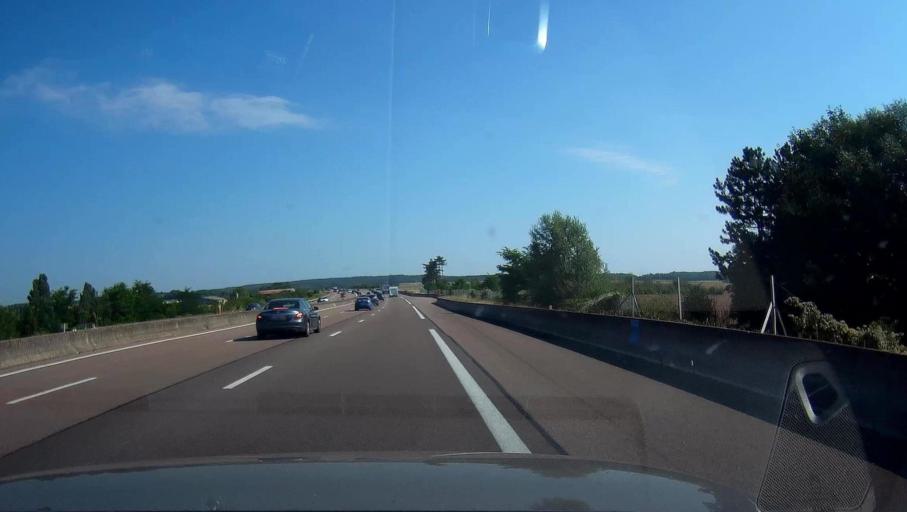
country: FR
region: Bourgogne
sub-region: Departement de la Cote-d'Or
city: Selongey
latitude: 47.5678
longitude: 5.2047
